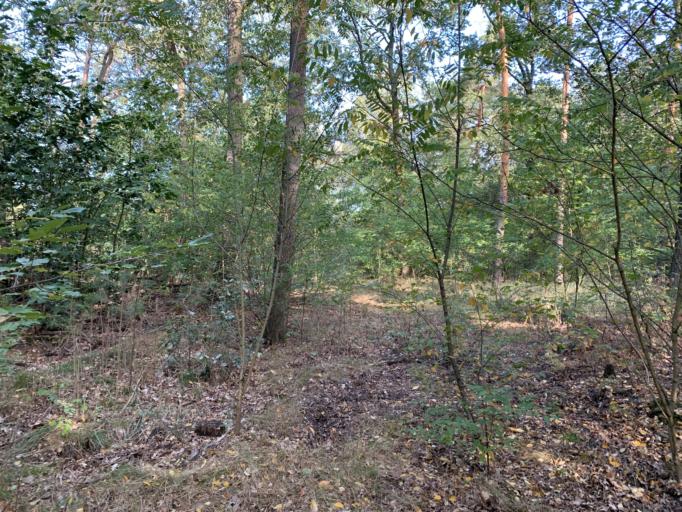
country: DE
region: Berlin
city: Wannsee
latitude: 52.4053
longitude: 13.1773
